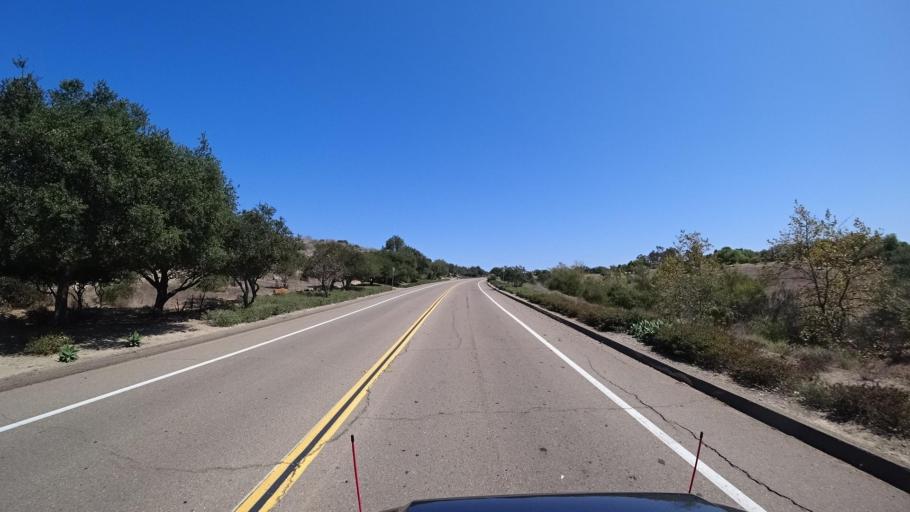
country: US
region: California
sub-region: San Diego County
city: Fairbanks Ranch
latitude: 33.0046
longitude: -117.1674
